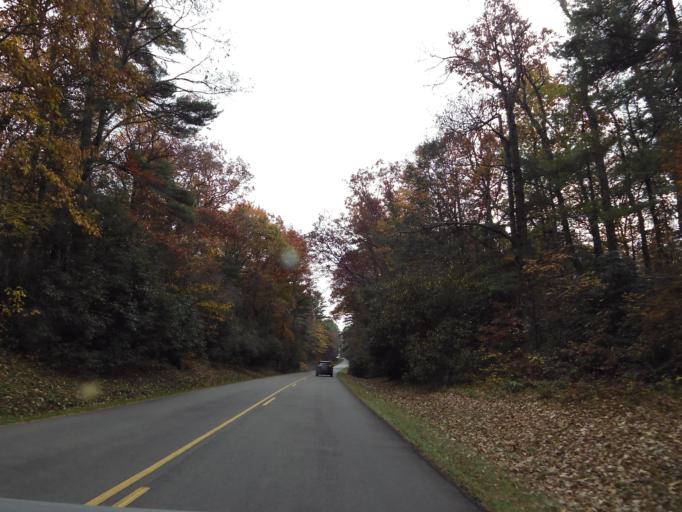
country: US
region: North Carolina
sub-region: Ashe County
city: Jefferson
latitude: 36.3499
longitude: -81.3732
